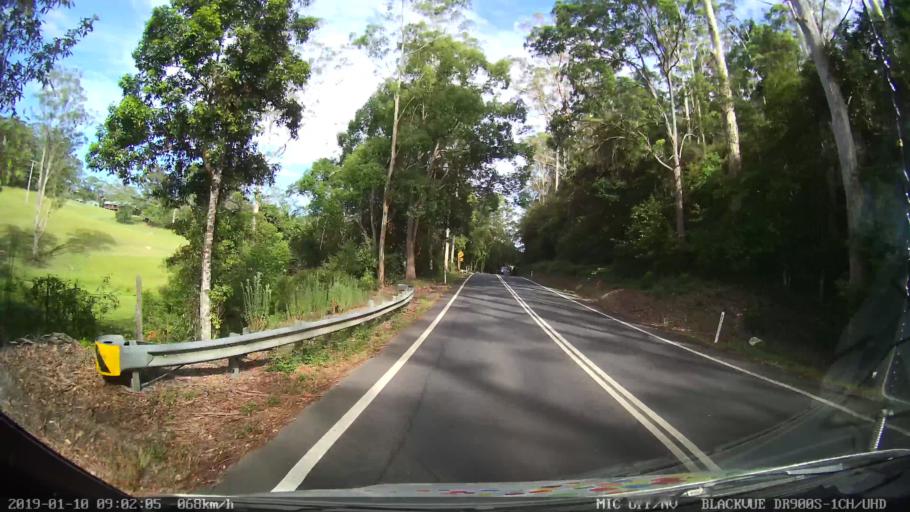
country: AU
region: New South Wales
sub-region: Coffs Harbour
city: Coffs Harbour
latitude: -30.2752
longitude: 153.0550
